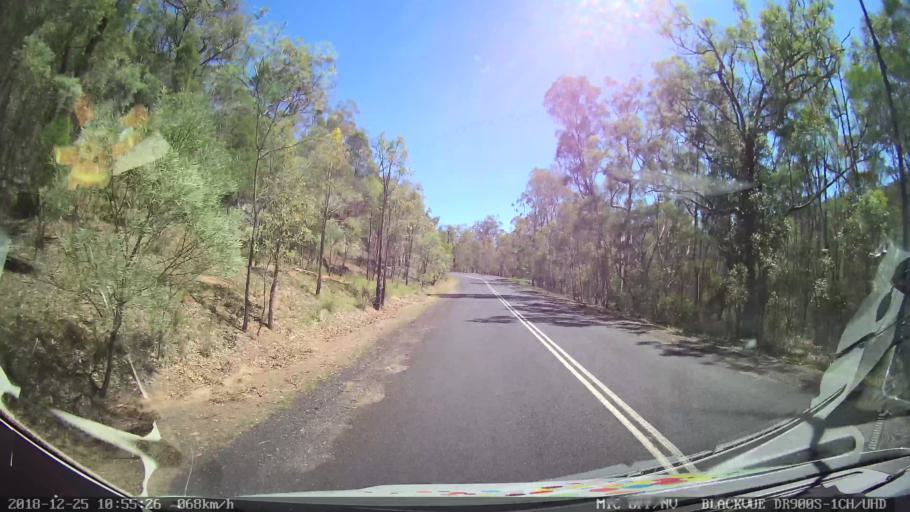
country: AU
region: New South Wales
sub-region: Upper Hunter Shire
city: Merriwa
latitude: -32.3991
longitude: 150.2722
